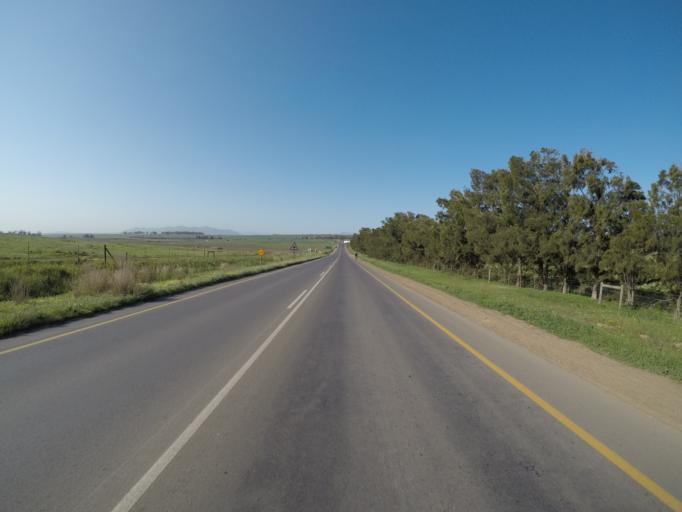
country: ZA
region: Western Cape
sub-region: City of Cape Town
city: Kraaifontein
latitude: -33.7723
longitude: 18.7528
